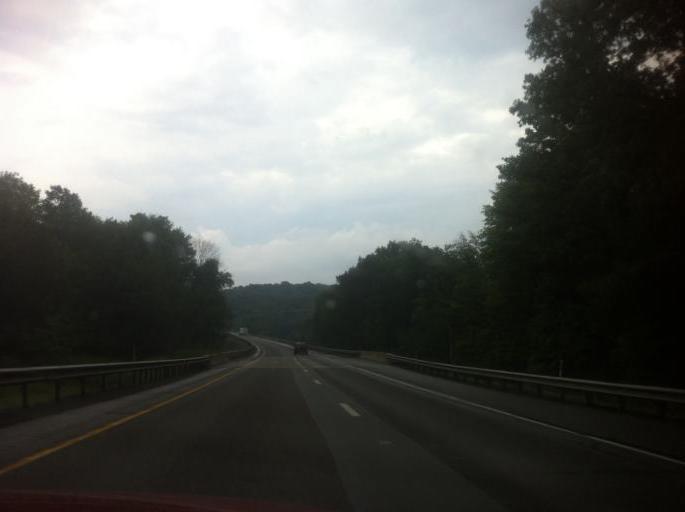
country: US
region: Pennsylvania
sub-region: Jefferson County
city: Brookville
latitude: 41.1578
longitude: -79.0000
